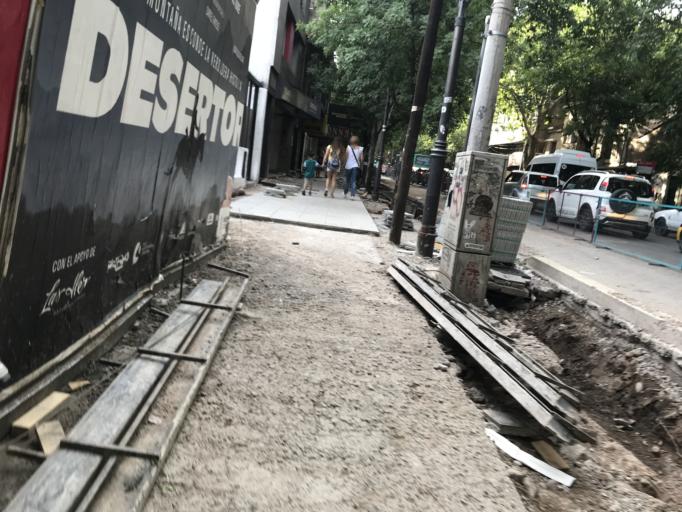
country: AR
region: Mendoza
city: Mendoza
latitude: -32.8931
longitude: -68.8387
